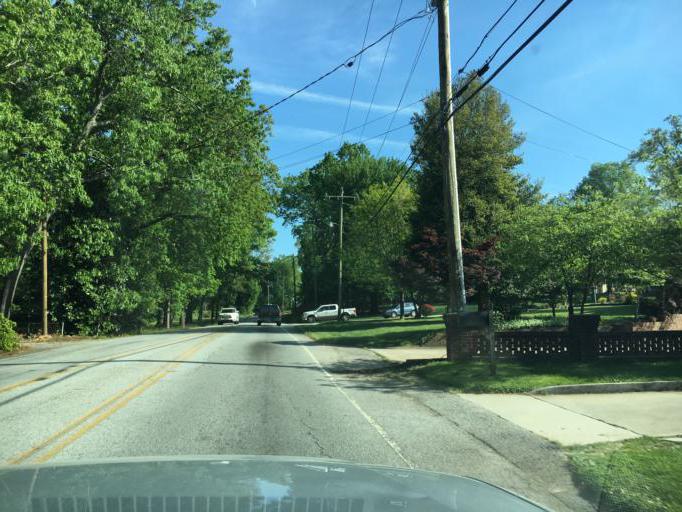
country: US
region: South Carolina
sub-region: Greenville County
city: Wade Hampton
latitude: 34.8860
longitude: -82.3305
